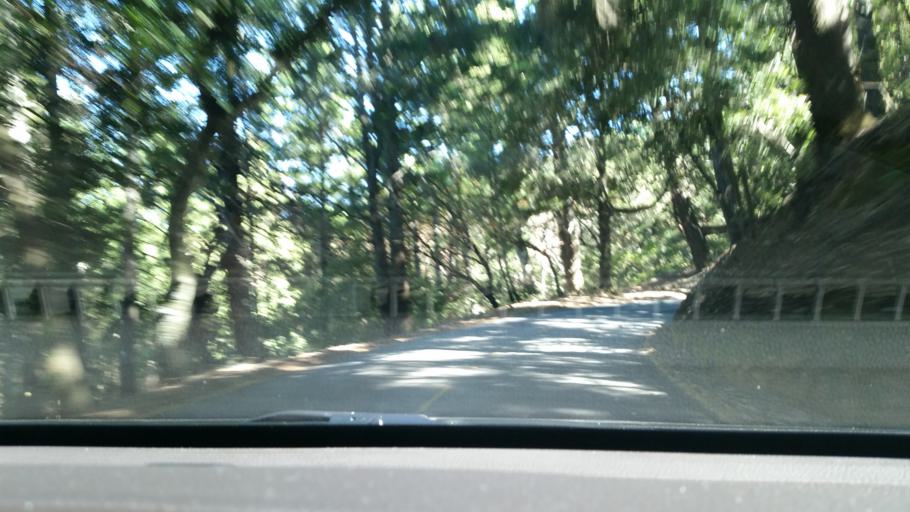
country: US
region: California
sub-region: San Mateo County
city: Woodside
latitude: 37.4274
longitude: -122.2993
